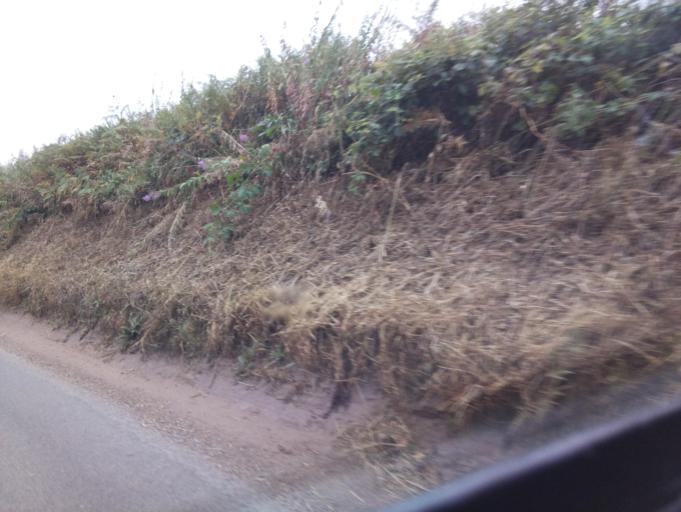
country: GB
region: England
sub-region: Derbyshire
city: Swadlincote
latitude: 52.7785
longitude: -1.5106
